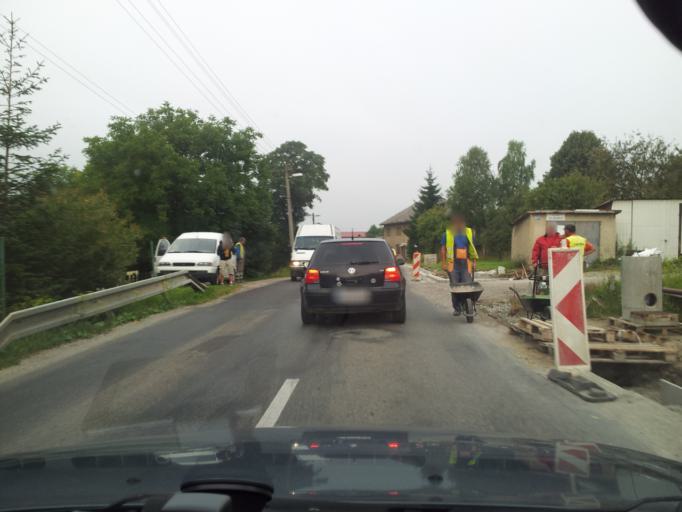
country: SK
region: Zilinsky
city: Cadca
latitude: 49.3951
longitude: 18.8600
